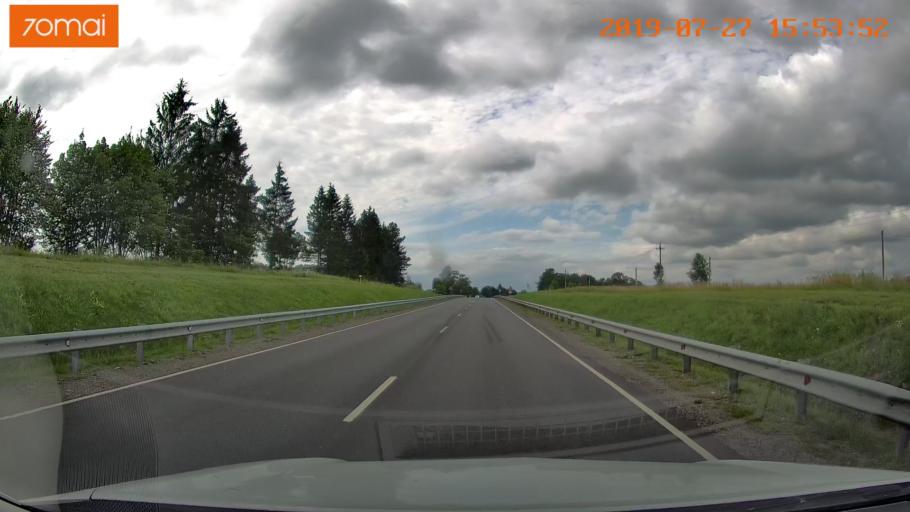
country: RU
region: Kaliningrad
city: Chernyakhovsk
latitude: 54.6051
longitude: 21.9471
